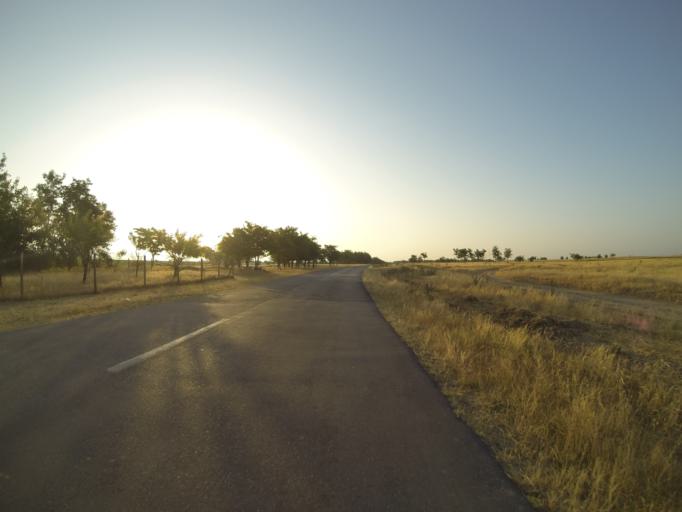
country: RO
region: Dolj
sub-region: Comuna Daneti
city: Daneti
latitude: 43.9721
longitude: 24.0678
